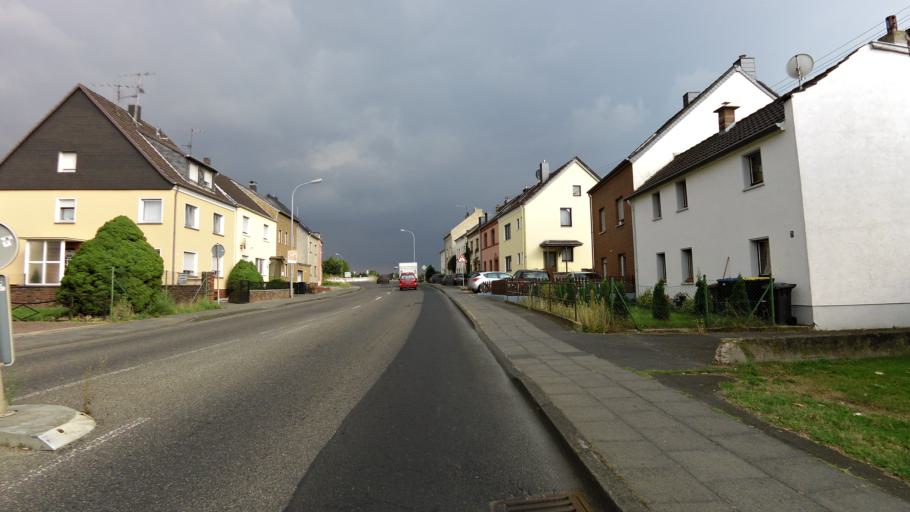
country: DE
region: North Rhine-Westphalia
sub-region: Regierungsbezirk Koln
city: Euskirchen
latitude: 50.6494
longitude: 6.8332
